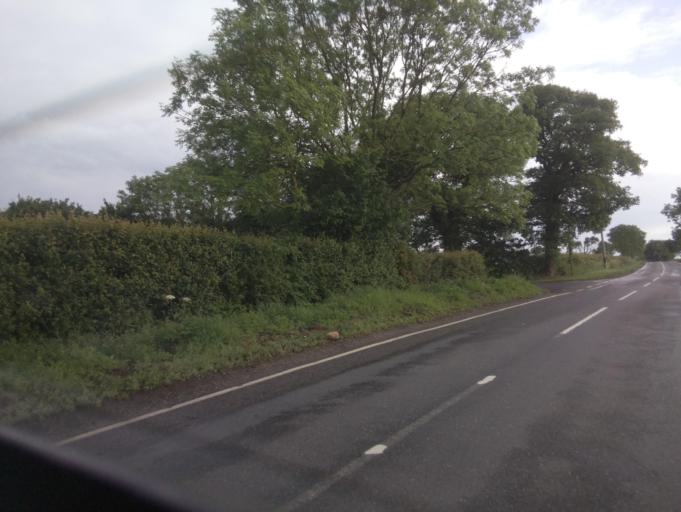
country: GB
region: England
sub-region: Lincolnshire
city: Great Gonerby
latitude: 53.0104
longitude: -0.6639
